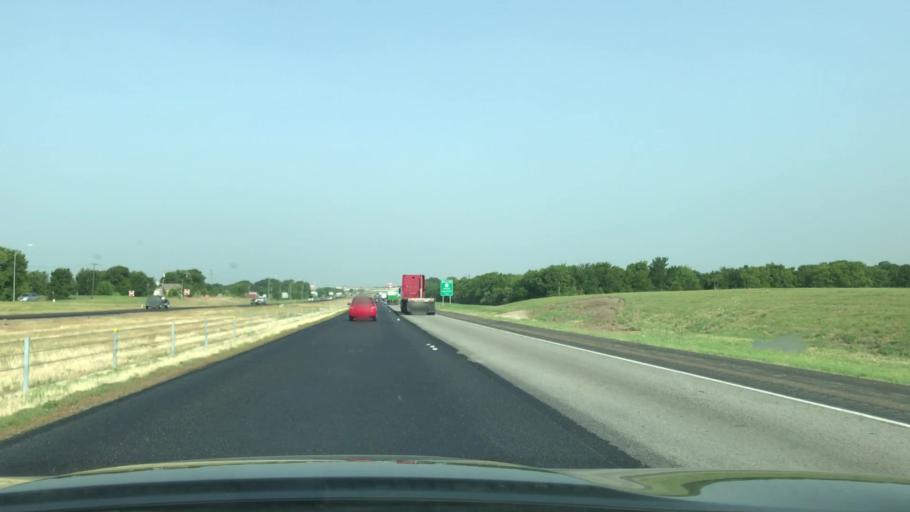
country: US
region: Texas
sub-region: Kaufman County
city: Terrell
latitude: 32.6952
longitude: -96.2520
